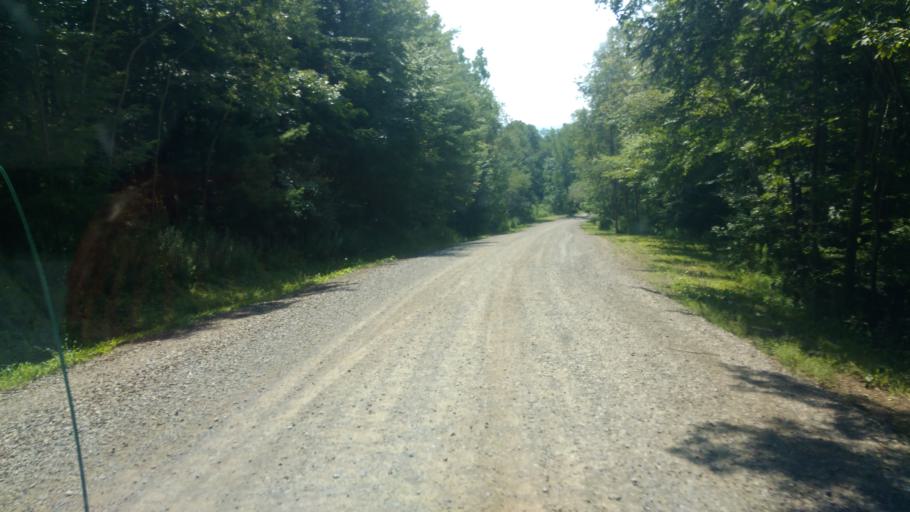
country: US
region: New York
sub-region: Steuben County
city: Canisteo
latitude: 42.3254
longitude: -77.5956
